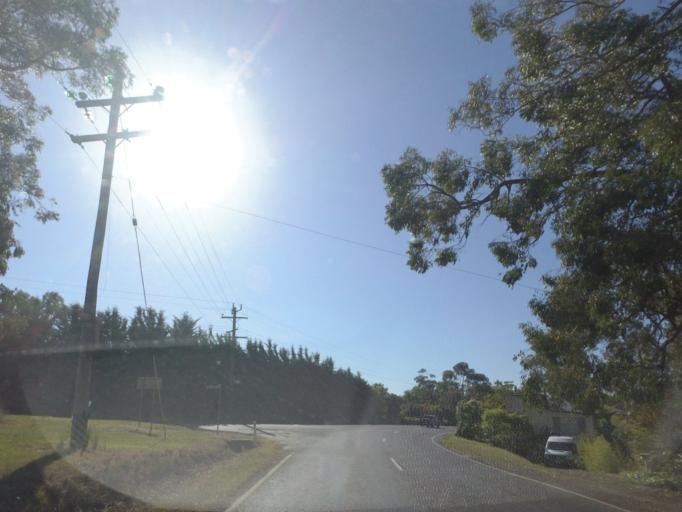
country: AU
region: Victoria
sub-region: Yarra Ranges
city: Yarra Junction
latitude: -37.8240
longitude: 145.6540
